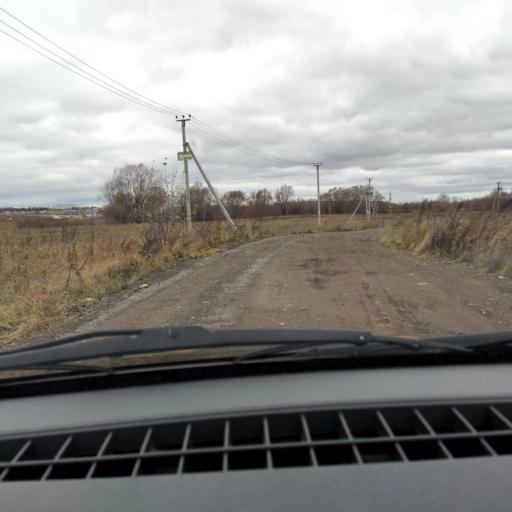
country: RU
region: Bashkortostan
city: Avdon
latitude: 54.5008
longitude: 55.8746
